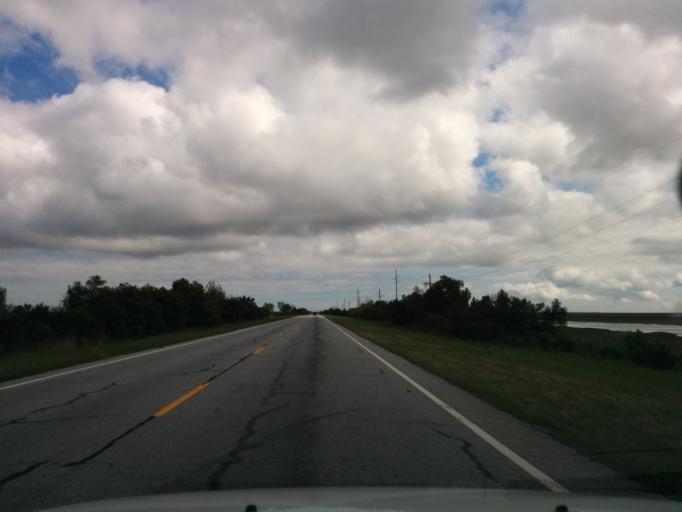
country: US
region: Georgia
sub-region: Glynn County
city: Brunswick
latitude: 31.0992
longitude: -81.4882
